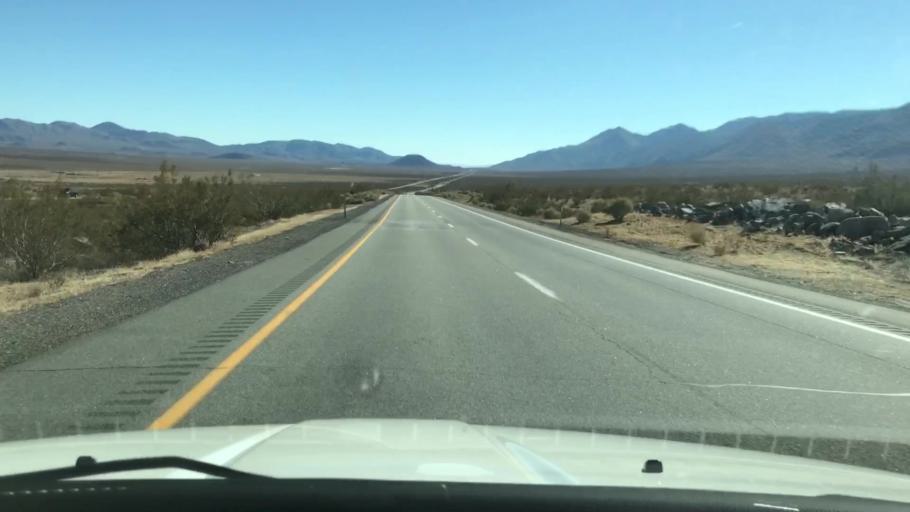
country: US
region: California
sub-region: Kern County
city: Inyokern
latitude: 36.0988
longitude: -117.9661
